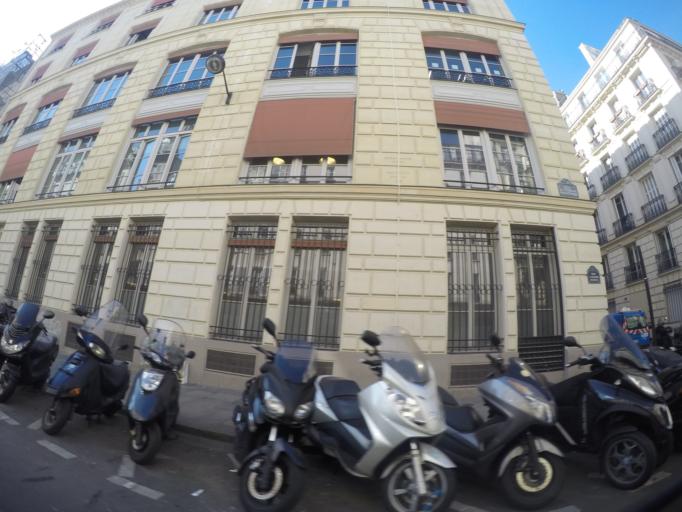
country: FR
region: Ile-de-France
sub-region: Paris
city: Saint-Ouen
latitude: 48.8803
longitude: 2.3497
